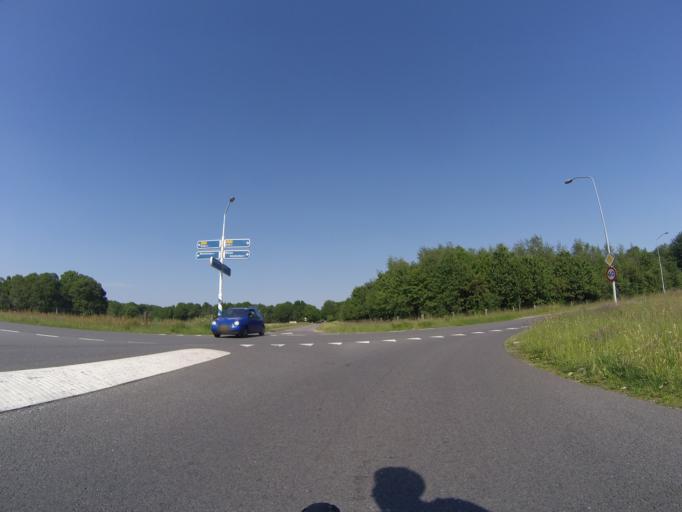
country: NL
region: Drenthe
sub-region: Gemeente Coevorden
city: Sleen
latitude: 52.7653
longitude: 6.8118
